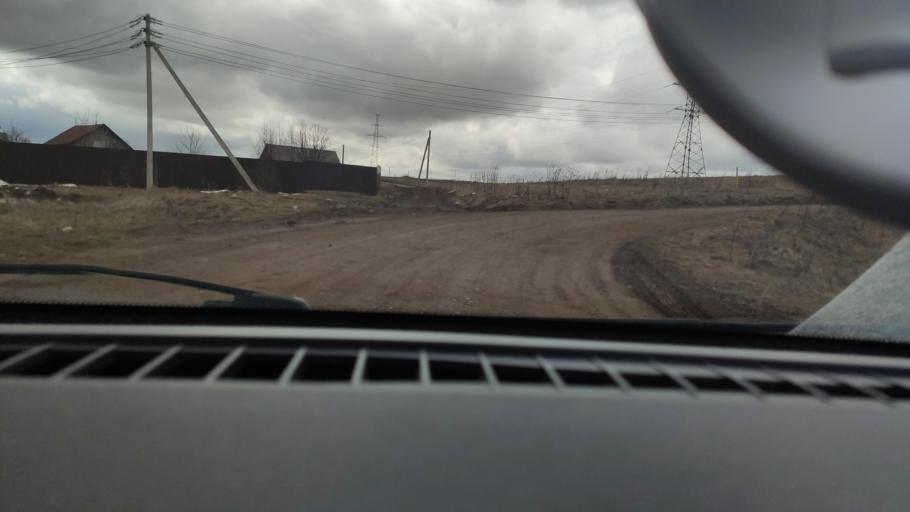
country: RU
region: Perm
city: Ferma
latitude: 57.9415
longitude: 56.3465
